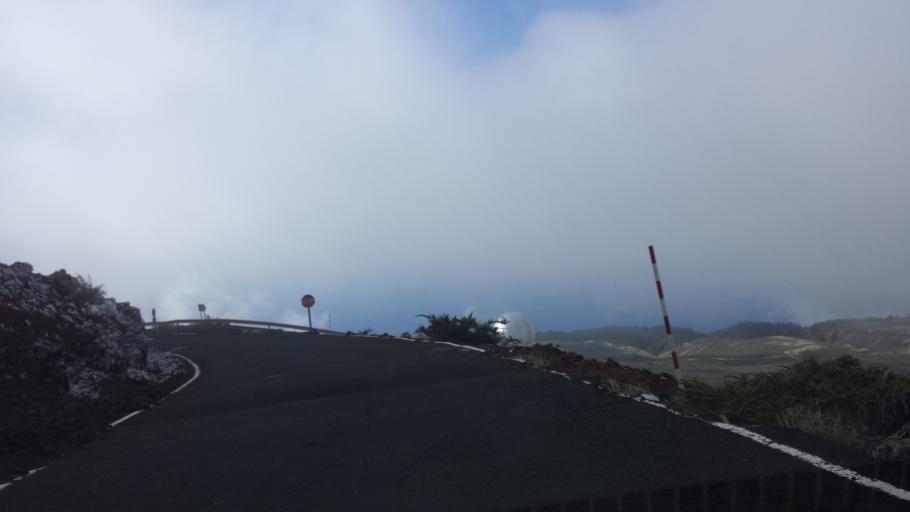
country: ES
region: Canary Islands
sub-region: Provincia de Santa Cruz de Tenerife
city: Garafia
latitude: 28.7551
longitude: -17.8852
